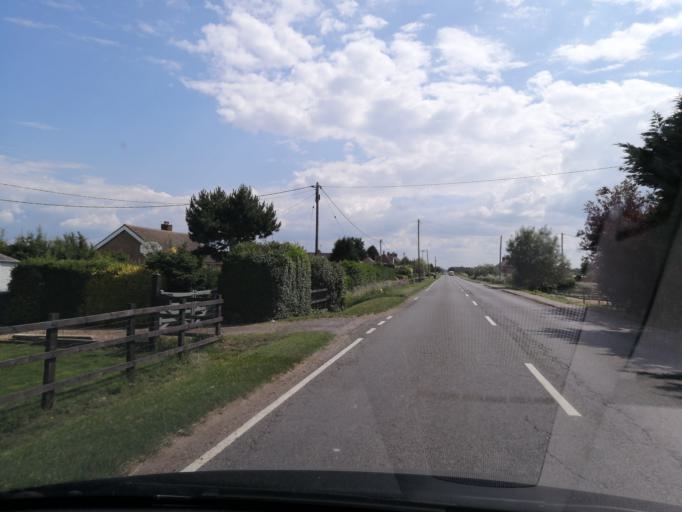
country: GB
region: England
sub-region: Cambridgeshire
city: Ramsey
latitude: 52.4869
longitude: -0.1494
